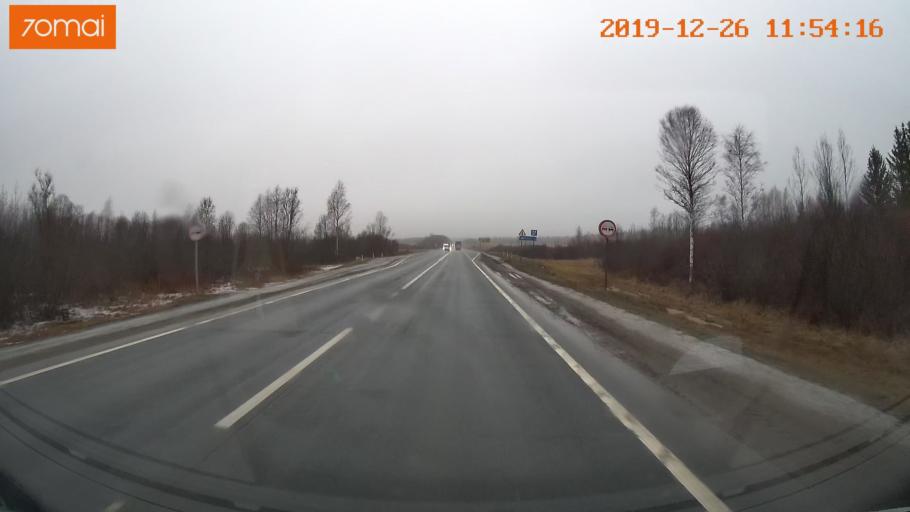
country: RU
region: Vologda
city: Sheksna
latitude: 59.2757
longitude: 38.3091
